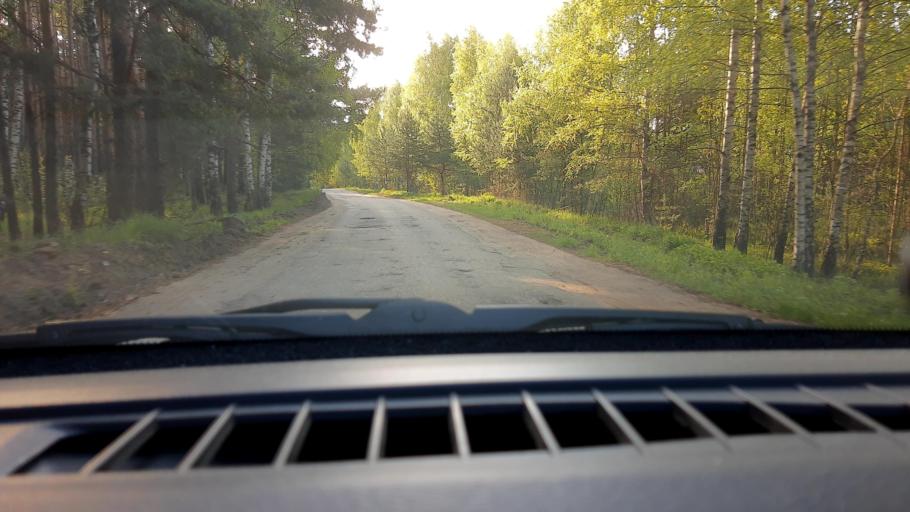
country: RU
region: Nizjnij Novgorod
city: Sitniki
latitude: 56.4147
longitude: 44.0517
